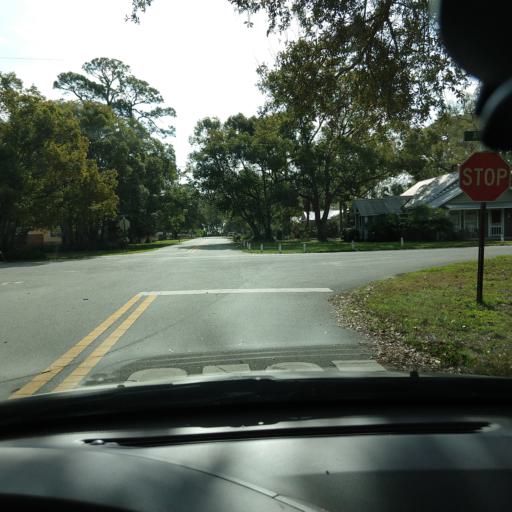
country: US
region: Florida
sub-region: Franklin County
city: Apalachicola
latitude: 29.7175
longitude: -84.9959
